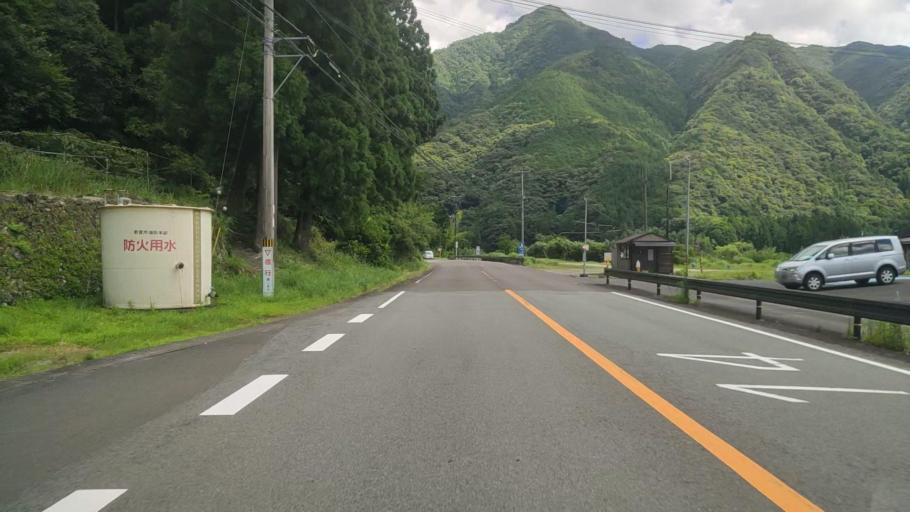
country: JP
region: Wakayama
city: Shingu
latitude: 33.7913
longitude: 135.8964
